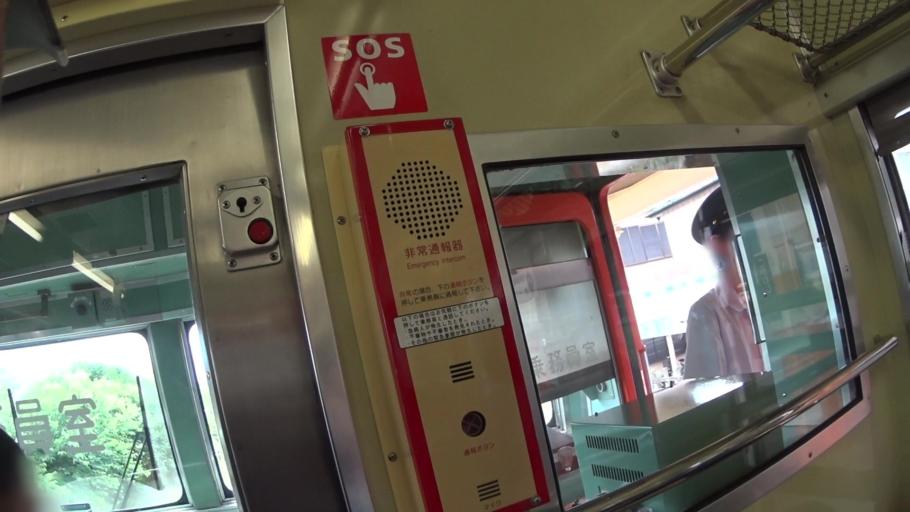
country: JP
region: Chiba
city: Nagareyama
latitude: 35.8393
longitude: 139.9135
